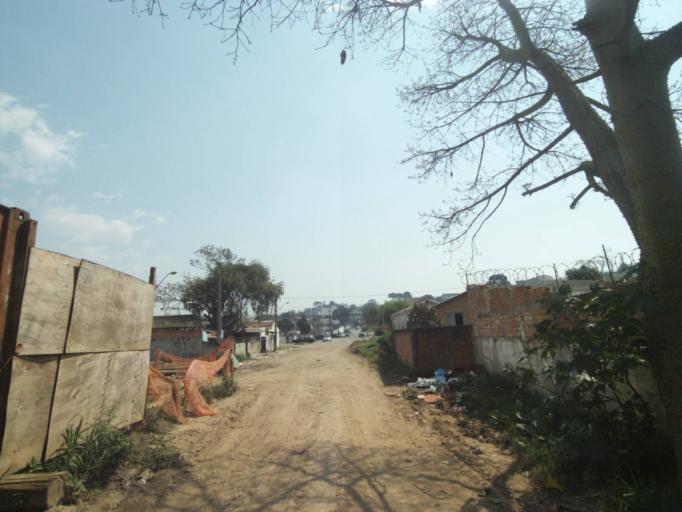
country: BR
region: Parana
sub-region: Curitiba
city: Curitiba
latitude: -25.4679
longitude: -49.2606
